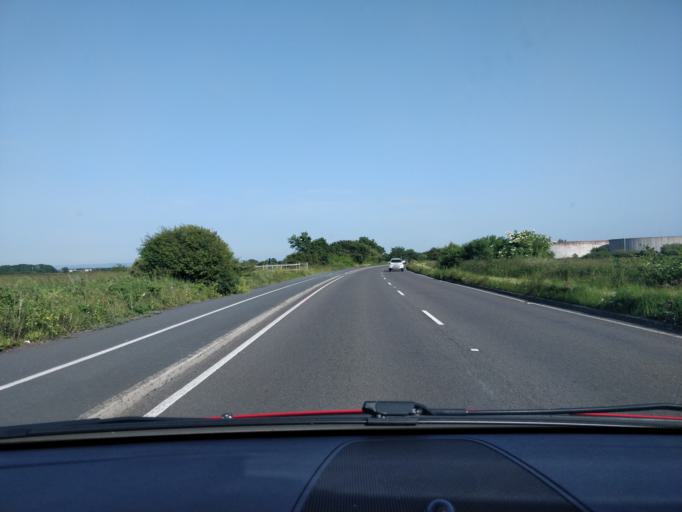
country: GB
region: England
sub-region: Lancashire
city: Banks
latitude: 53.6823
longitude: -2.9571
